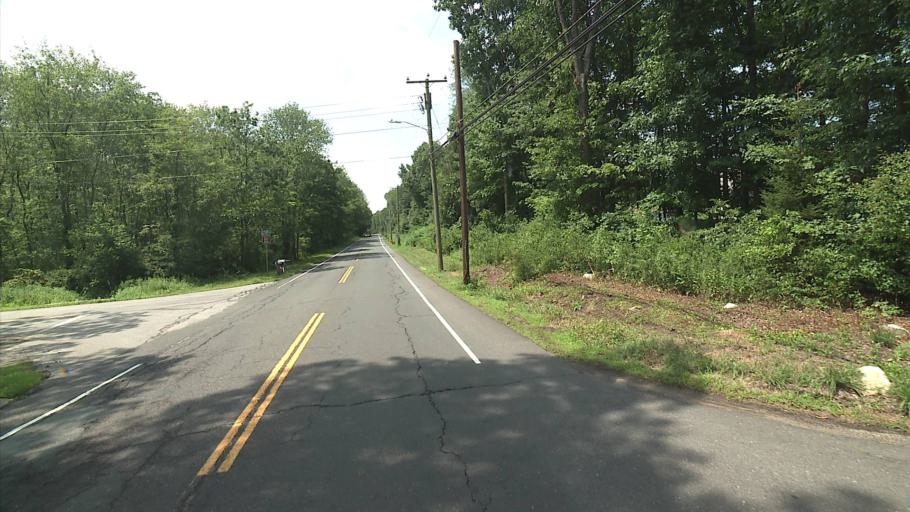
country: US
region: Connecticut
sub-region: Tolland County
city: Coventry Lake
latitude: 41.7877
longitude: -72.3422
